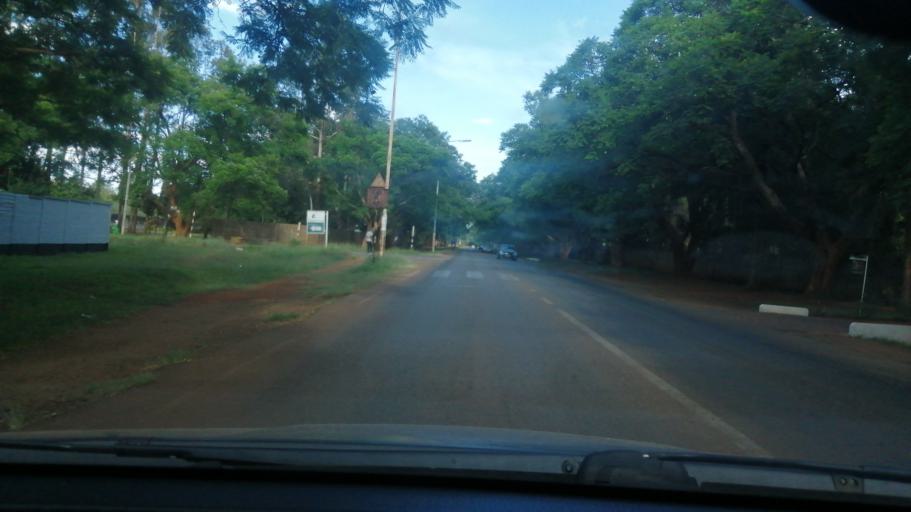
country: ZW
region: Harare
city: Harare
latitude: -17.7623
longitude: 31.0769
